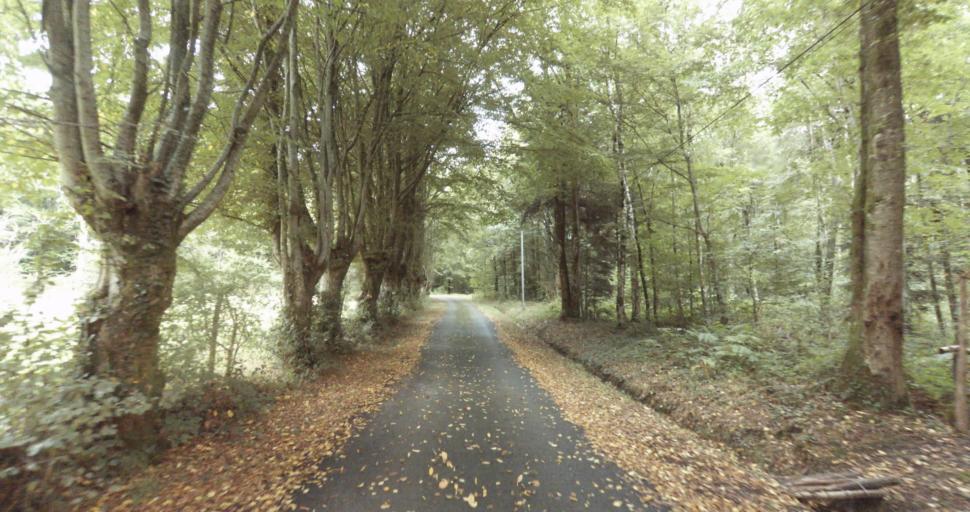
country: FR
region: Lower Normandy
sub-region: Departement de l'Orne
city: Sainte-Gauburge-Sainte-Colombe
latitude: 48.7530
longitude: 0.4385
